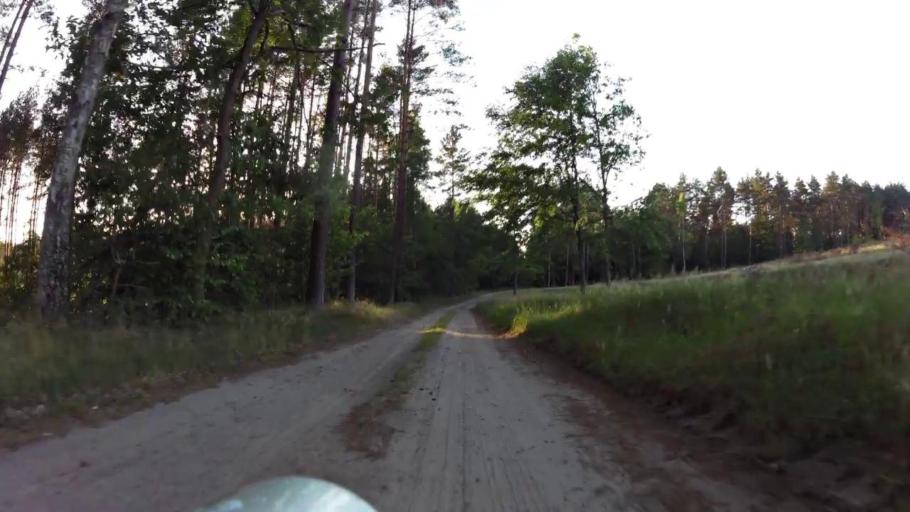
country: PL
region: West Pomeranian Voivodeship
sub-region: Powiat szczecinecki
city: Szczecinek
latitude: 53.8258
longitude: 16.6909
